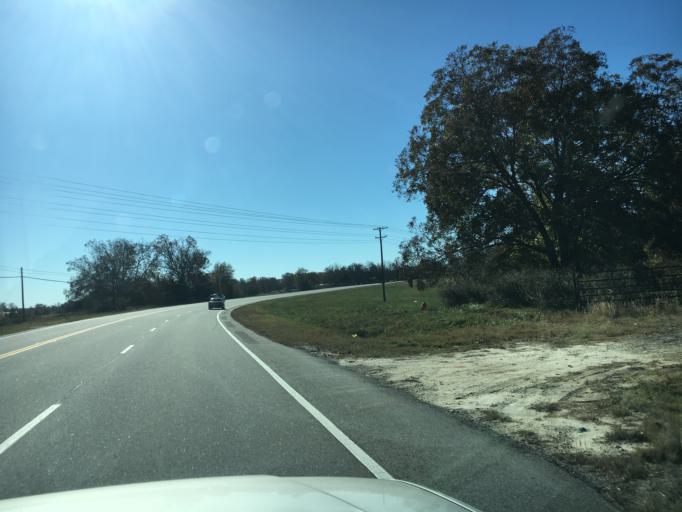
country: US
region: Georgia
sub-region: Hart County
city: Hartwell
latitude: 34.3217
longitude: -82.9791
